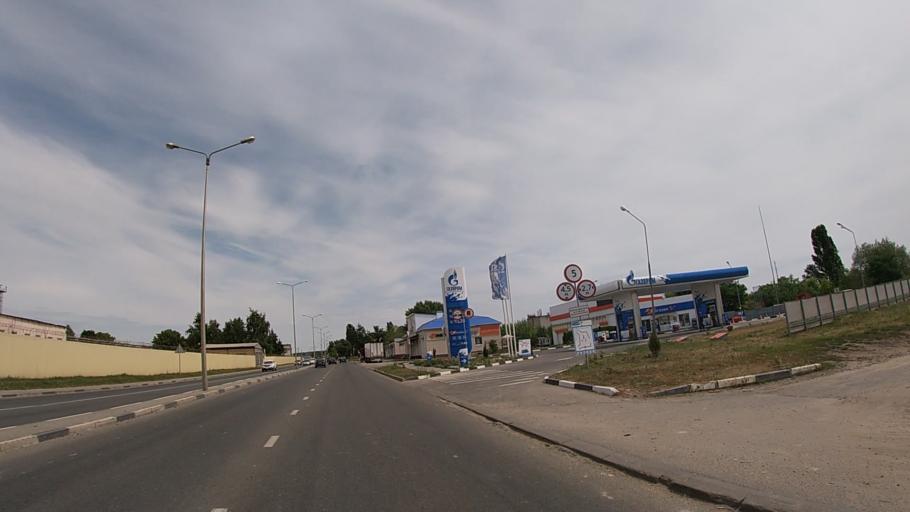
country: RU
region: Belgorod
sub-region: Belgorodskiy Rayon
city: Belgorod
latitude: 50.6157
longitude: 36.5377
